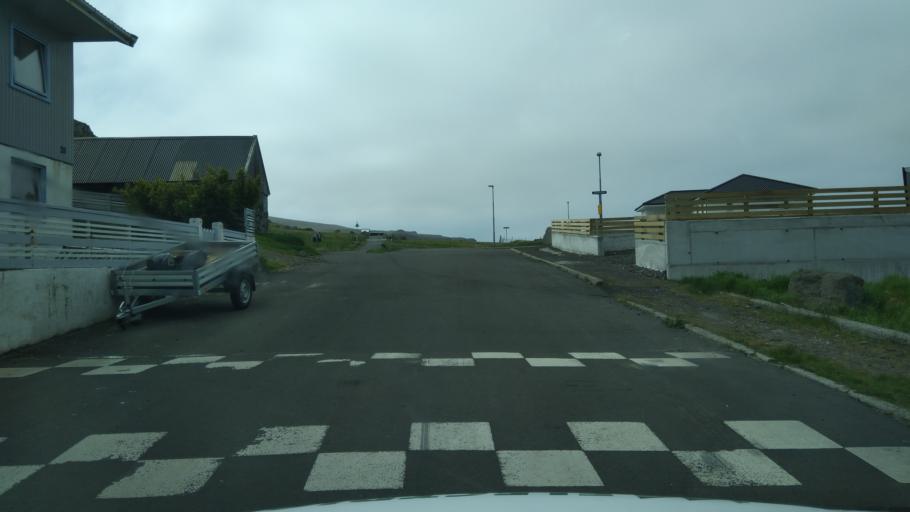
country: FO
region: Sandoy
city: Sandur
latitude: 61.9036
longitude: -6.8920
